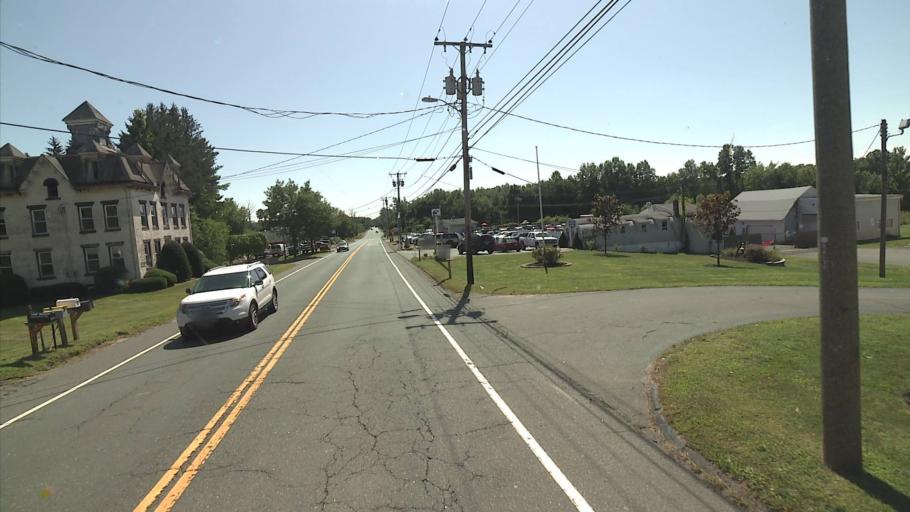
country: US
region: Connecticut
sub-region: Hartford County
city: Windsor Locks
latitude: 41.9506
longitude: -72.6279
